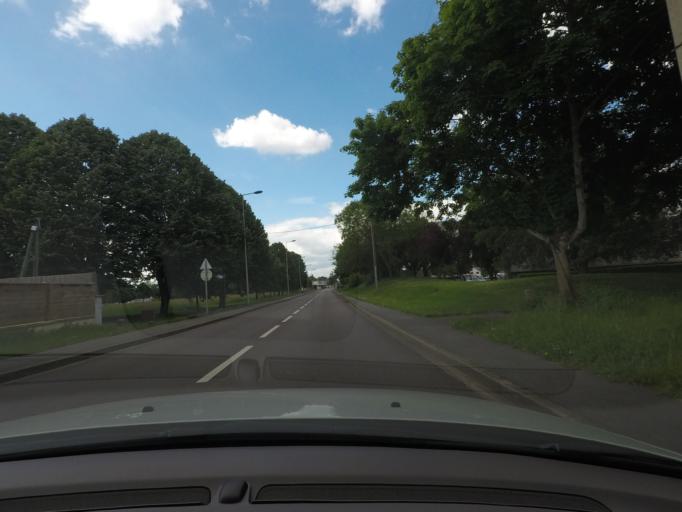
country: FR
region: Haute-Normandie
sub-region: Departement de l'Eure
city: Evreux
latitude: 49.0054
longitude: 1.1512
